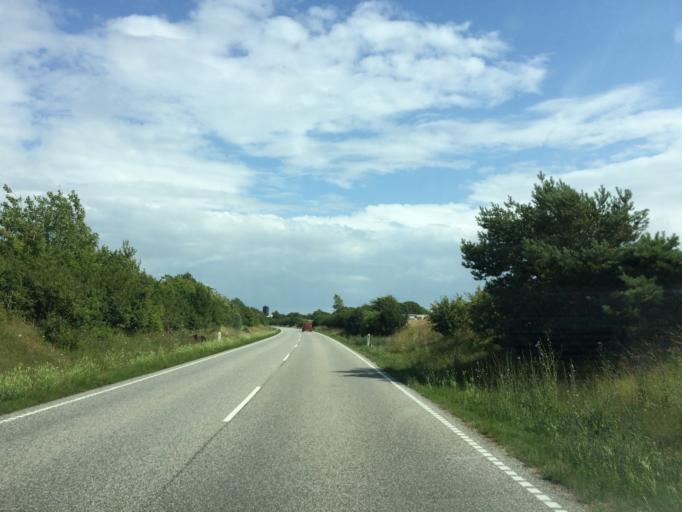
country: DK
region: Zealand
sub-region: Odsherred Kommune
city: Asnaes
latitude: 55.9633
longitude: 11.3661
